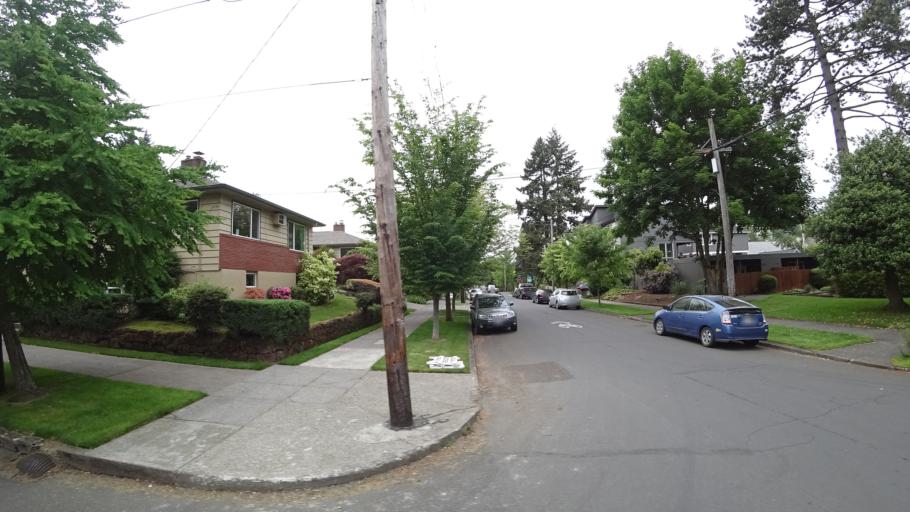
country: US
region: Oregon
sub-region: Multnomah County
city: Lents
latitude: 45.5026
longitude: -122.6205
